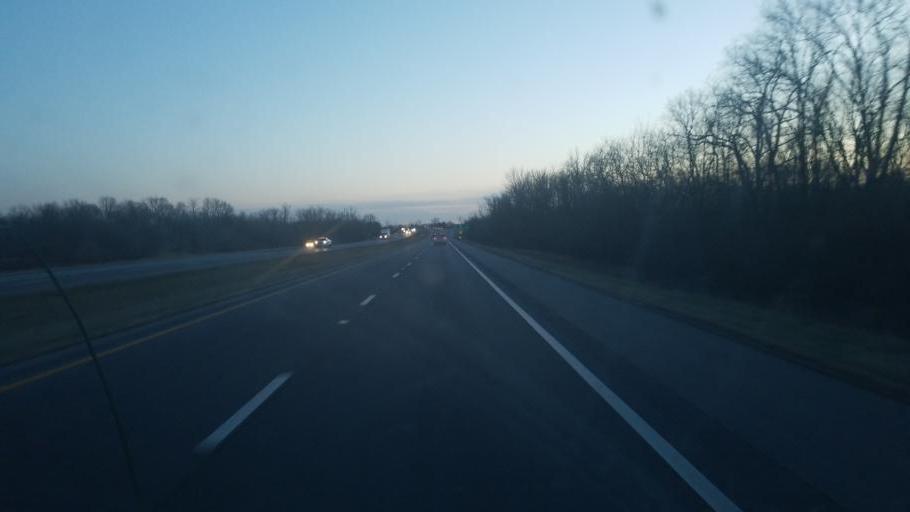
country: US
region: Ohio
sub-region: Marion County
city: Prospect
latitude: 40.4693
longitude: -83.0752
